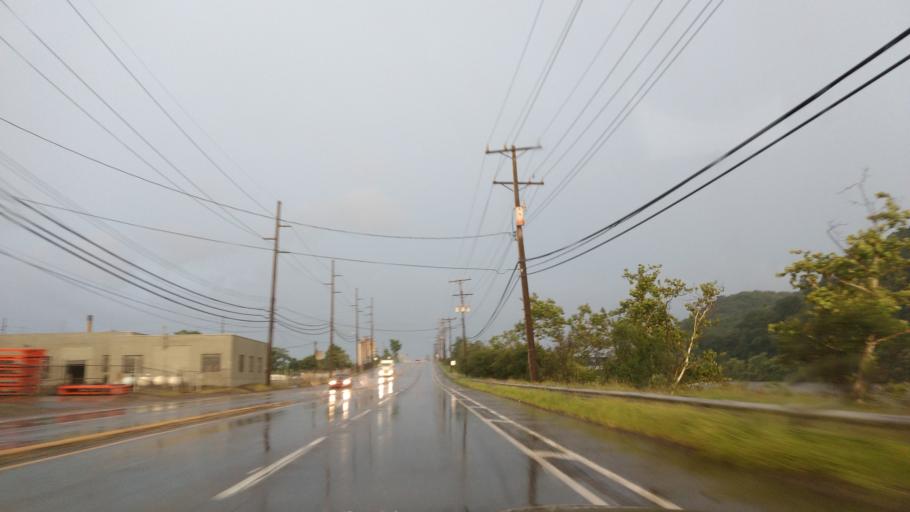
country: US
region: Pennsylvania
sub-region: Allegheny County
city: Ben Avon
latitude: 40.4952
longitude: -80.0862
